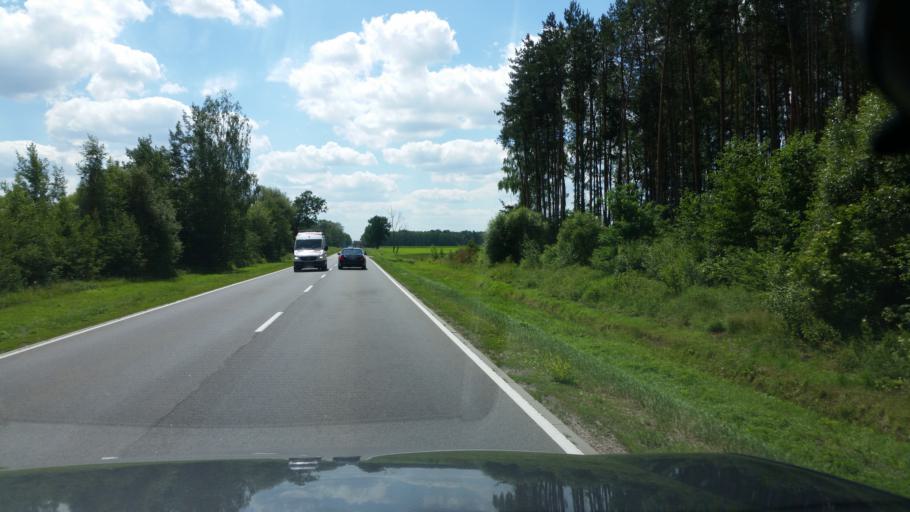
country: PL
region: Masovian Voivodeship
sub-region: Powiat ostrowski
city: Ostrow Mazowiecka
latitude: 52.9085
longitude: 21.8735
